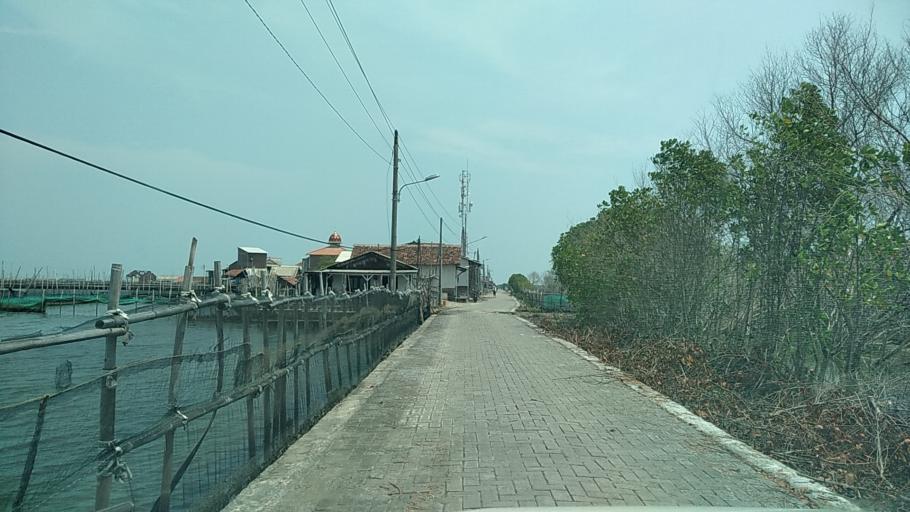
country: ID
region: Central Java
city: Semarang
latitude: -6.9486
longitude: 110.4406
